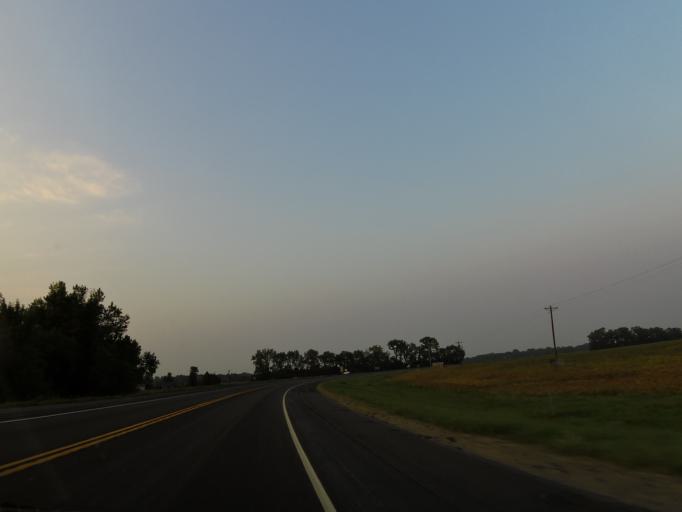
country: US
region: North Dakota
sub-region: Walsh County
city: Park River
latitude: 48.4090
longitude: -97.6224
